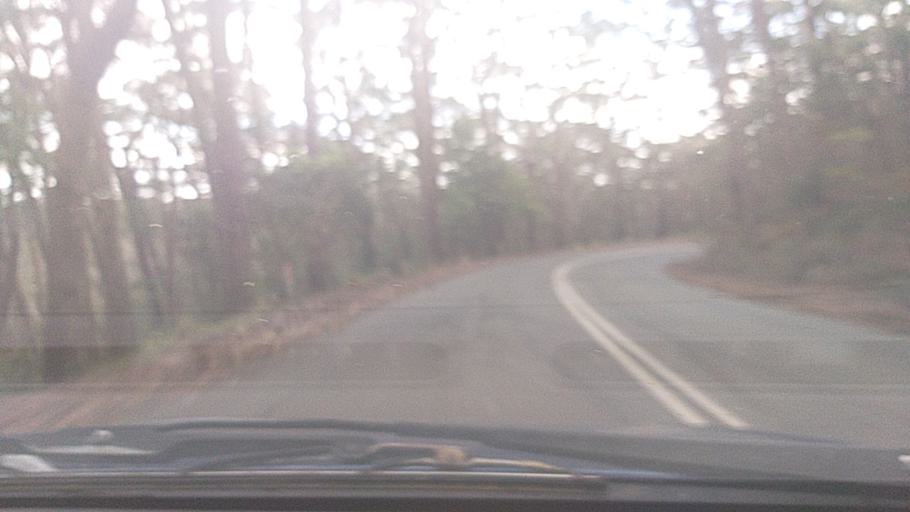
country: AU
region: New South Wales
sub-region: Wollongong
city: Mount Ousley
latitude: -34.3886
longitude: 150.8504
